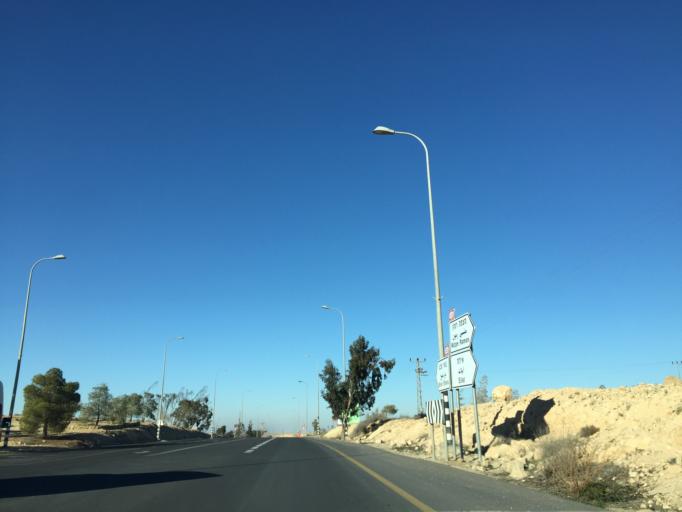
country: IL
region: Southern District
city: Mitzpe Ramon
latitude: 30.6158
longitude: 34.8036
